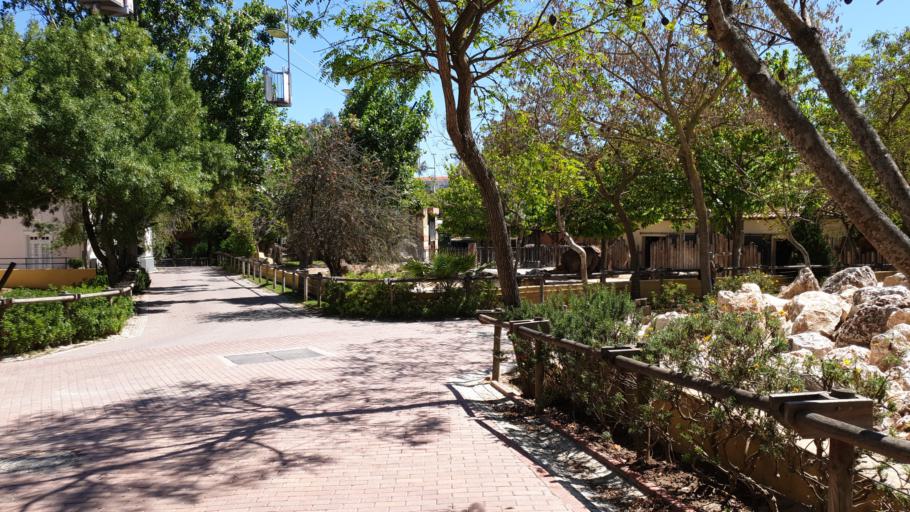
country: PT
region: Lisbon
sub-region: Odivelas
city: Pontinha
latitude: 38.7439
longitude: -9.1723
